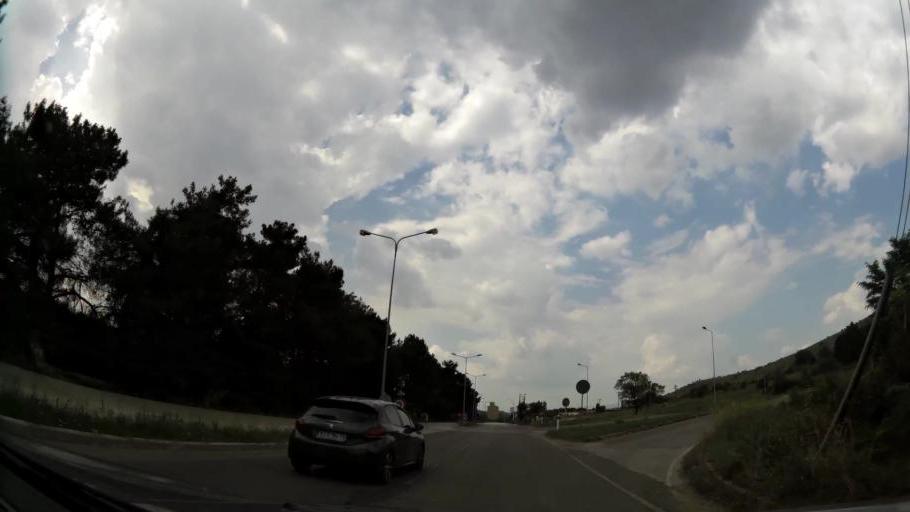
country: GR
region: West Macedonia
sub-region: Nomos Kozanis
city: Koila
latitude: 40.3333
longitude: 21.8265
